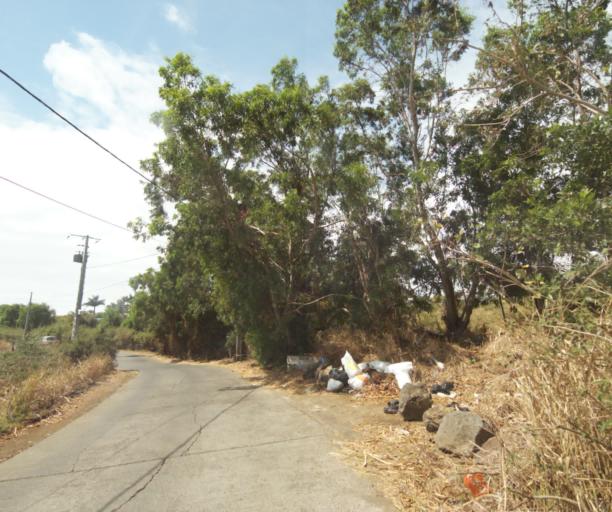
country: RE
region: Reunion
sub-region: Reunion
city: Trois-Bassins
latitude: -21.0643
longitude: 55.2645
